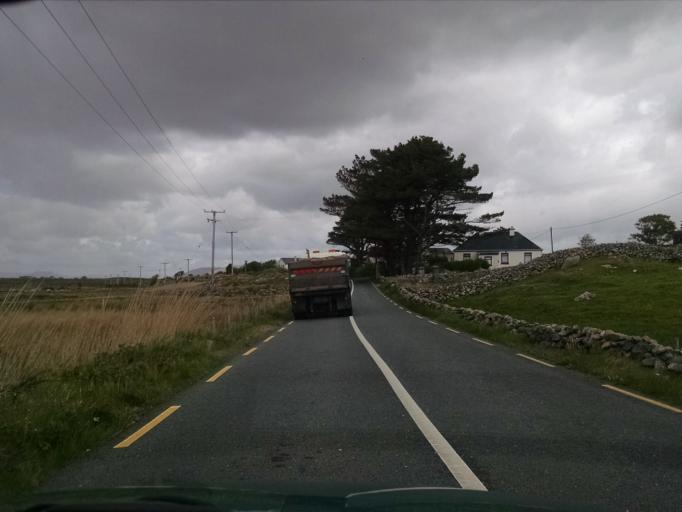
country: IE
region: Connaught
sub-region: County Galway
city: Oughterard
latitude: 53.3115
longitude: -9.5538
